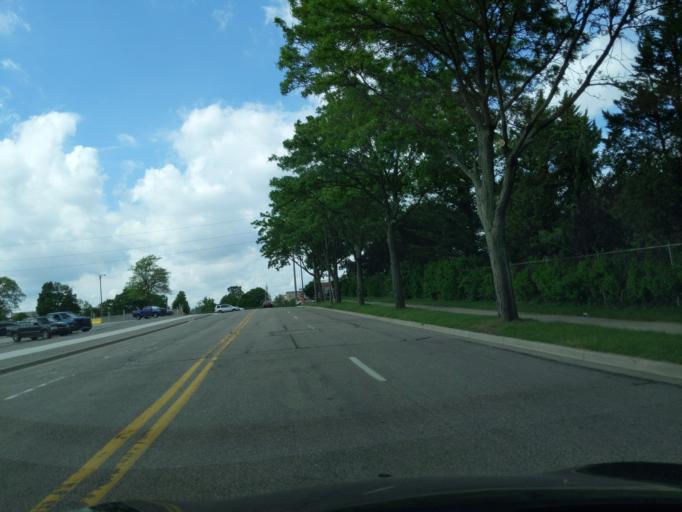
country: US
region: Michigan
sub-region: Ingham County
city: Lansing
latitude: 42.7245
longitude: -84.5555
